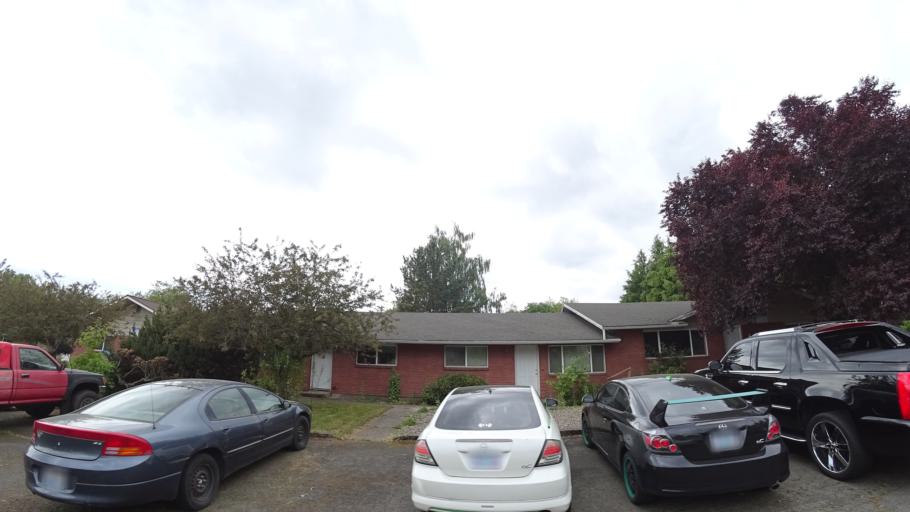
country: US
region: Oregon
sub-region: Washington County
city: Beaverton
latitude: 45.4935
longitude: -122.7947
